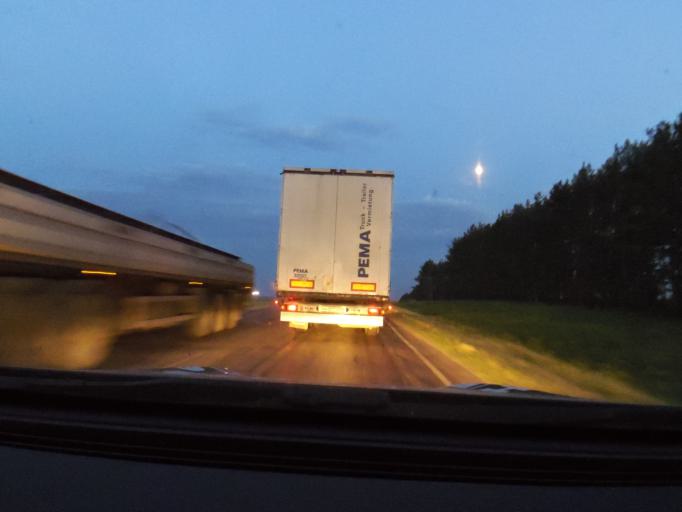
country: RU
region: Bashkortostan
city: Duvan
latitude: 56.0416
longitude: 58.2064
